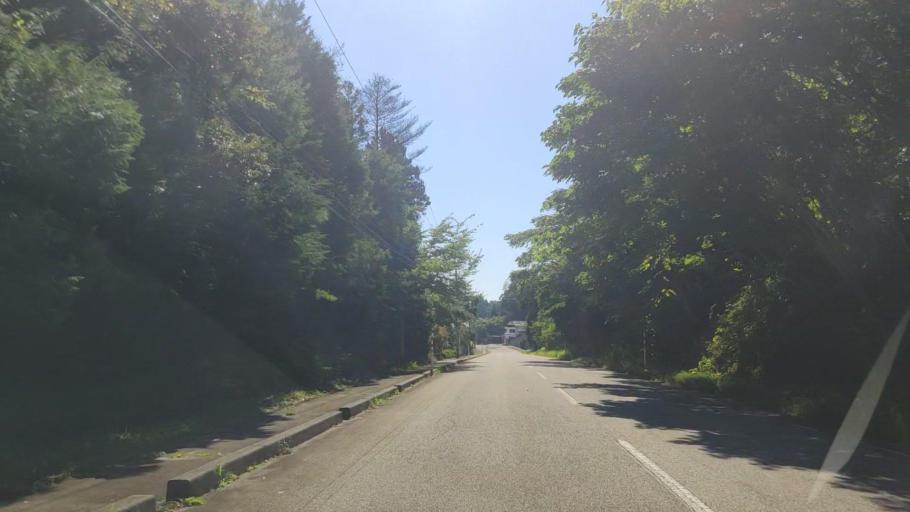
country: JP
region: Ishikawa
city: Nanao
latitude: 37.4688
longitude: 137.3234
